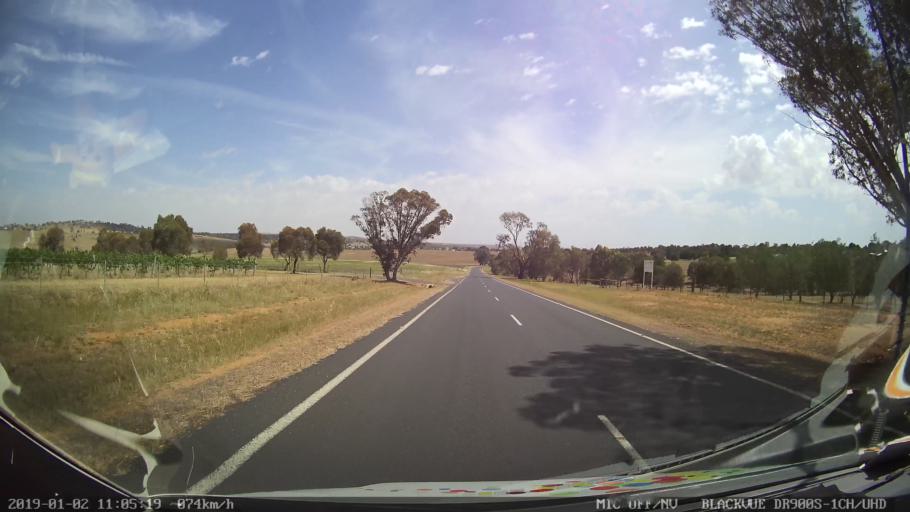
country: AU
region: New South Wales
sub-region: Young
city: Young
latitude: -34.5663
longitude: 148.3540
